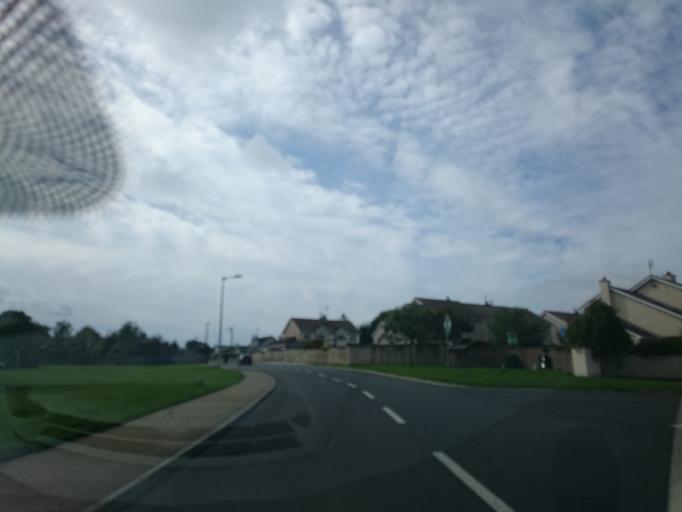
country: IE
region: Munster
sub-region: Waterford
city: Tra Mhor
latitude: 52.1696
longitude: -7.1541
